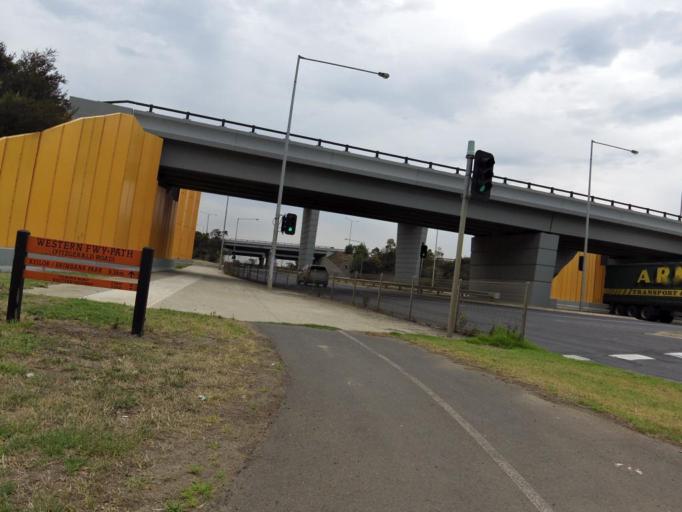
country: AU
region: Victoria
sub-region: Brimbank
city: Derrimut
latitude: -37.8001
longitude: 144.7889
